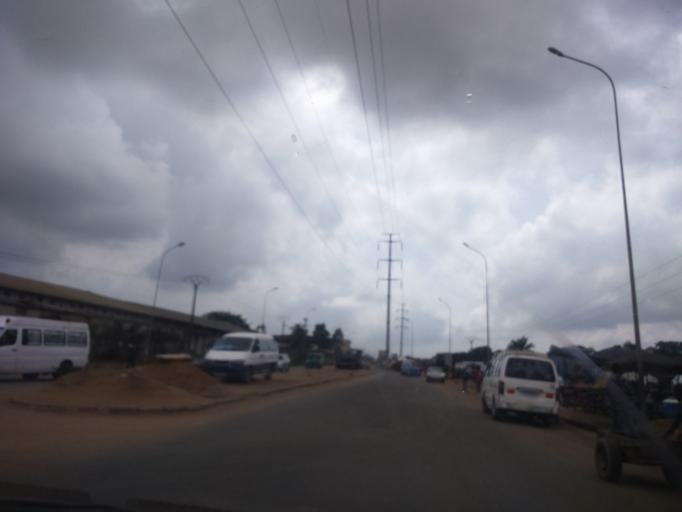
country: CI
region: Lagunes
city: Abobo
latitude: 5.3743
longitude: -4.0777
